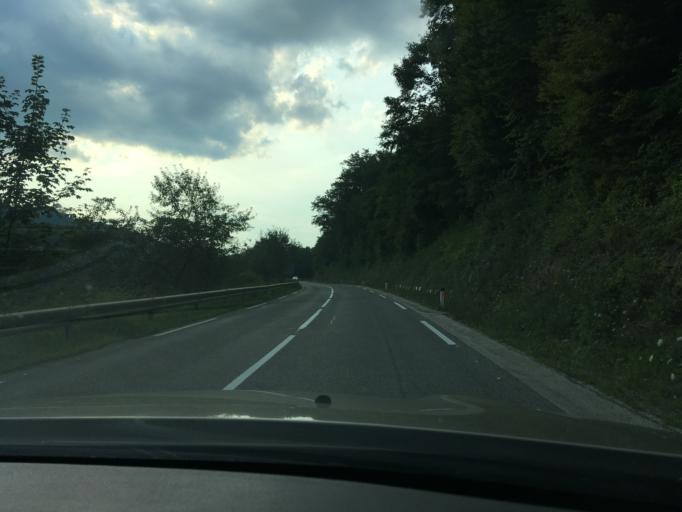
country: SI
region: Dolenjske Toplice
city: Dolenjske Toplice
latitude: 45.7865
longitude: 14.9948
